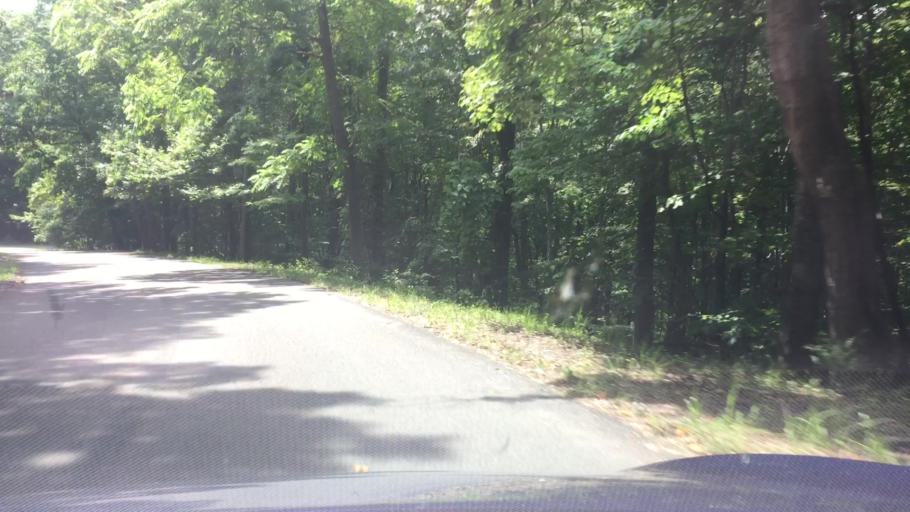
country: US
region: Virginia
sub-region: Wythe County
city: Wytheville
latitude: 36.9265
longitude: -81.0570
